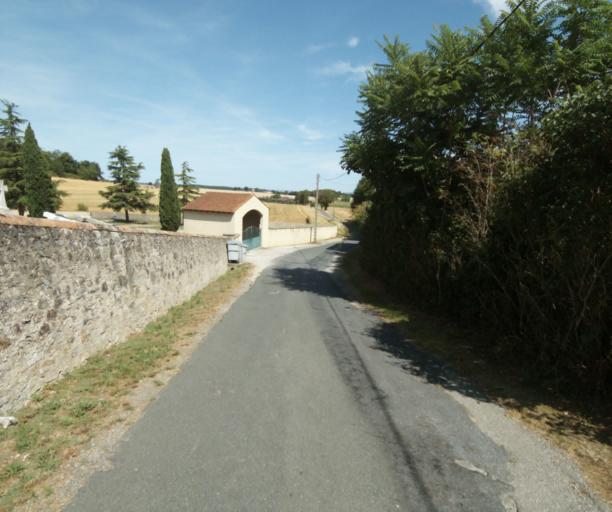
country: FR
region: Midi-Pyrenees
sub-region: Departement du Tarn
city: Puylaurens
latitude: 43.5263
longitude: 2.0087
